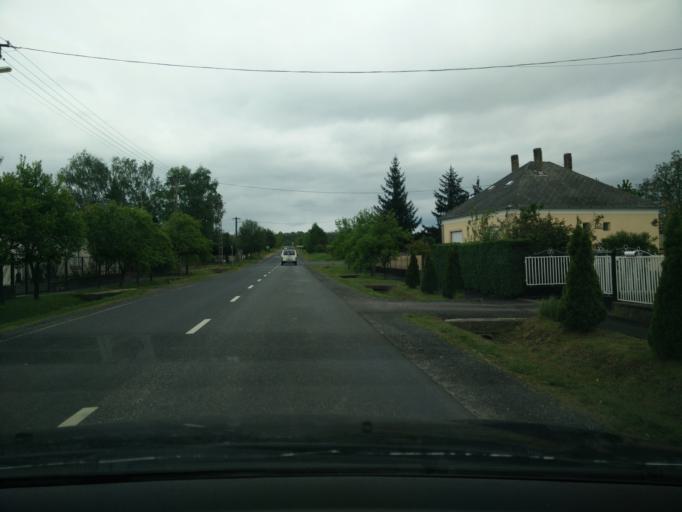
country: HU
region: Zala
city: Turje
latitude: 46.9820
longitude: 17.1141
